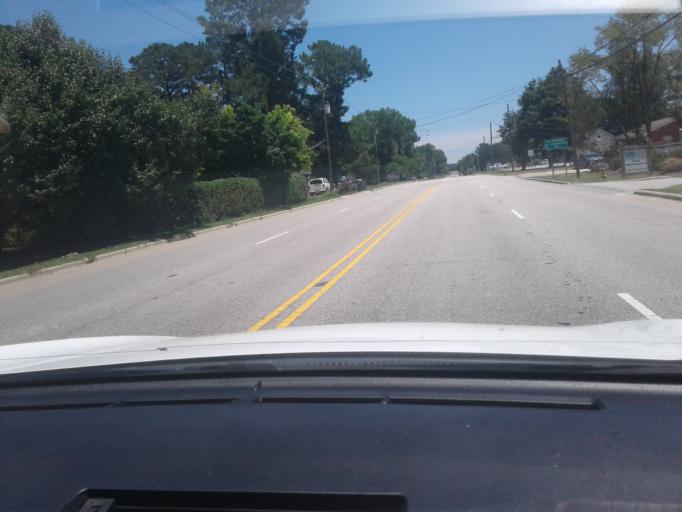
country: US
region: North Carolina
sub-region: Harnett County
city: Lillington
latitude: 35.3907
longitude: -78.8037
